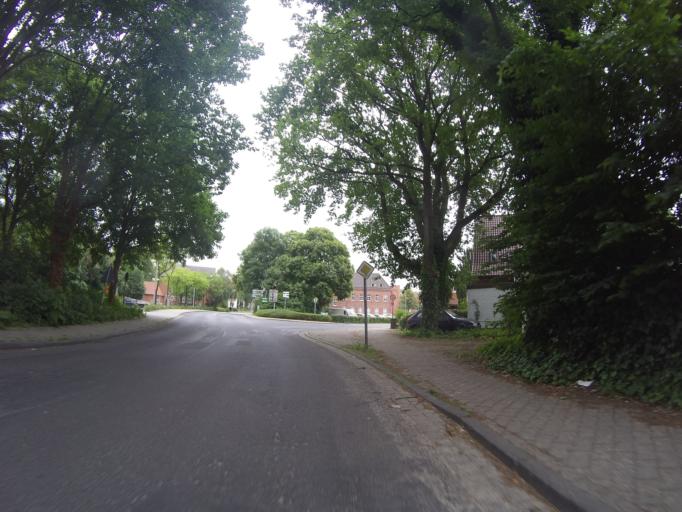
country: DE
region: Lower Saxony
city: Meppen
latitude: 52.6960
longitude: 7.2928
